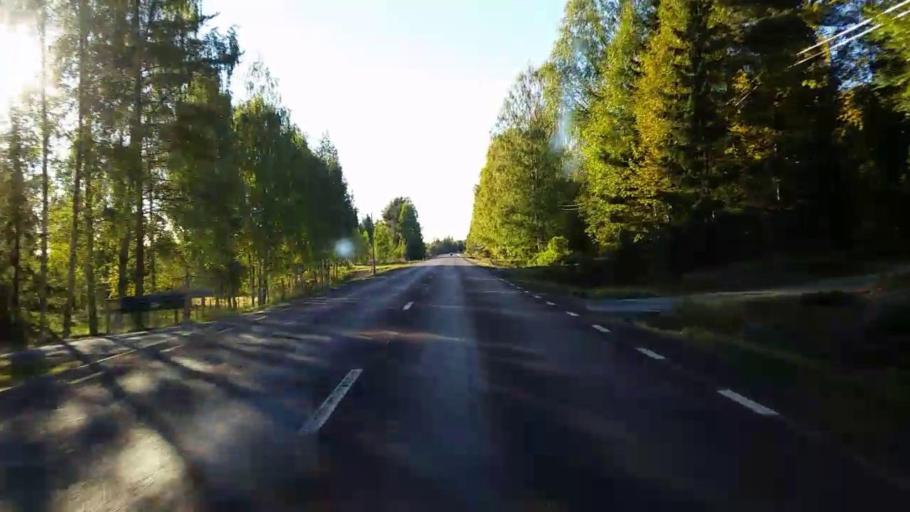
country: SE
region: Gaevleborg
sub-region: Ljusdals Kommun
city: Ljusdal
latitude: 61.8186
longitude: 16.1788
